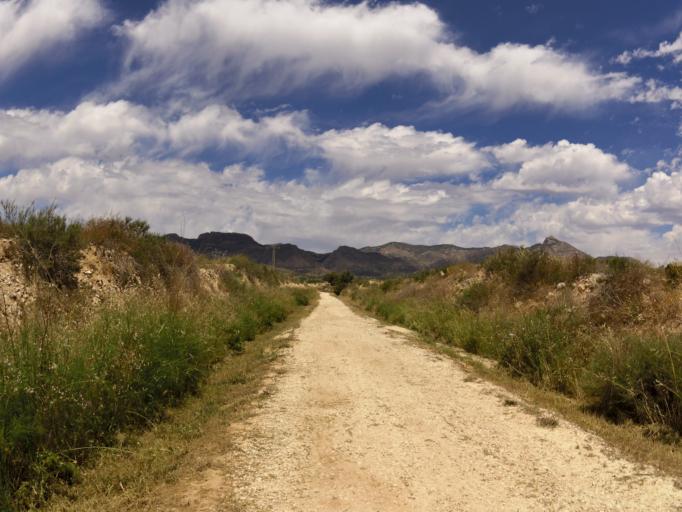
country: ES
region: Valencia
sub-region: Provincia de Alicante
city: Agost
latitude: 38.4472
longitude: -0.6672
